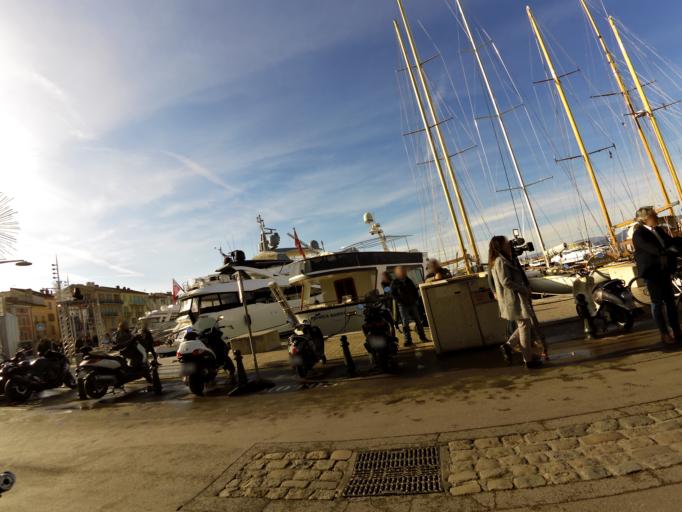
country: FR
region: Provence-Alpes-Cote d'Azur
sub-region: Departement du Var
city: Saint-Tropez
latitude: 43.2720
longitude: 6.6390
